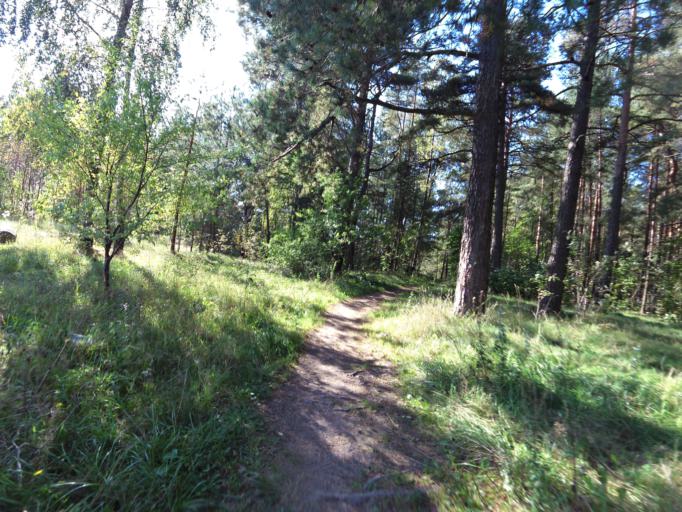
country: LT
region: Vilnius County
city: Pilaite
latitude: 54.6875
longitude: 25.1948
